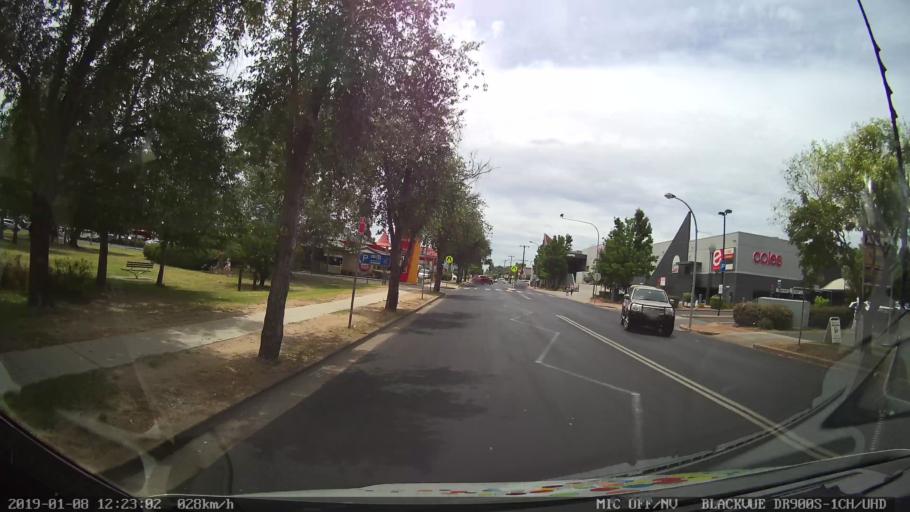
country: AU
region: New South Wales
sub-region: Armidale Dumaresq
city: Armidale
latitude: -30.5125
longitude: 151.6679
